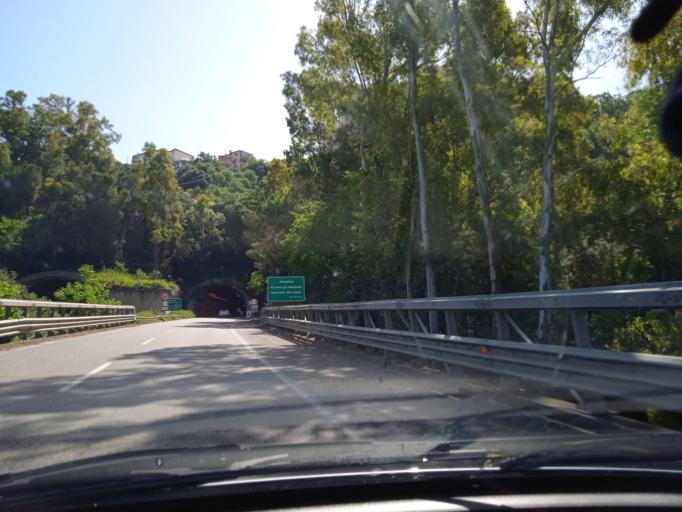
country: IT
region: Sicily
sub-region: Messina
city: Brolo
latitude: 38.1524
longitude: 14.8353
